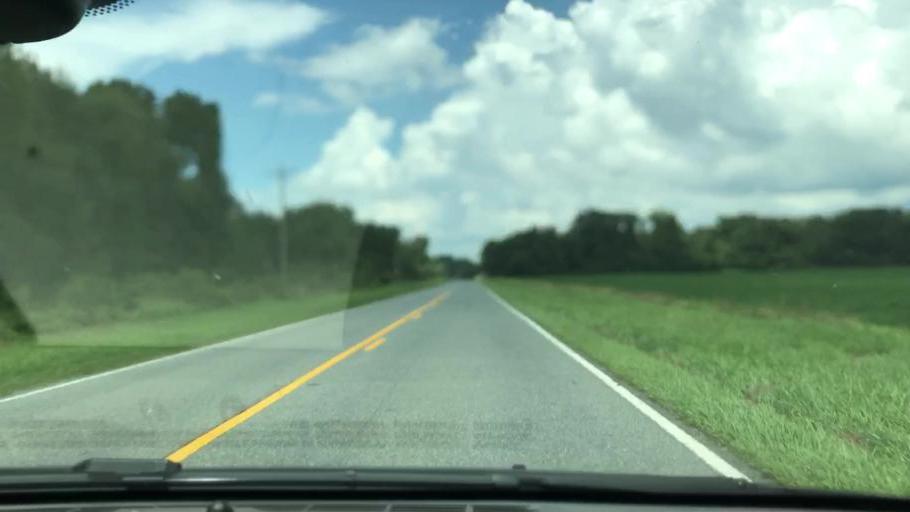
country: US
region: Florida
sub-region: Jackson County
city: Malone
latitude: 30.9525
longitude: -85.1182
